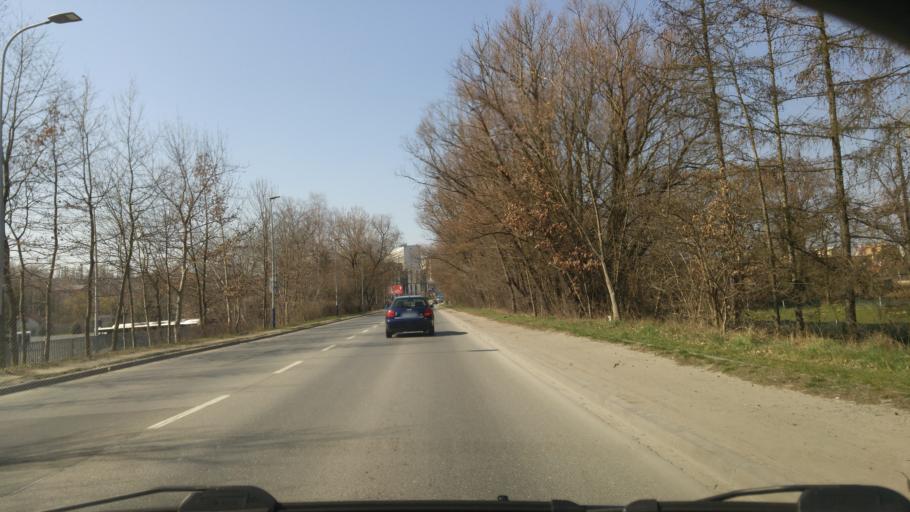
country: PL
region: Lesser Poland Voivodeship
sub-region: Powiat krakowski
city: Michalowice
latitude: 50.0934
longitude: 20.0321
